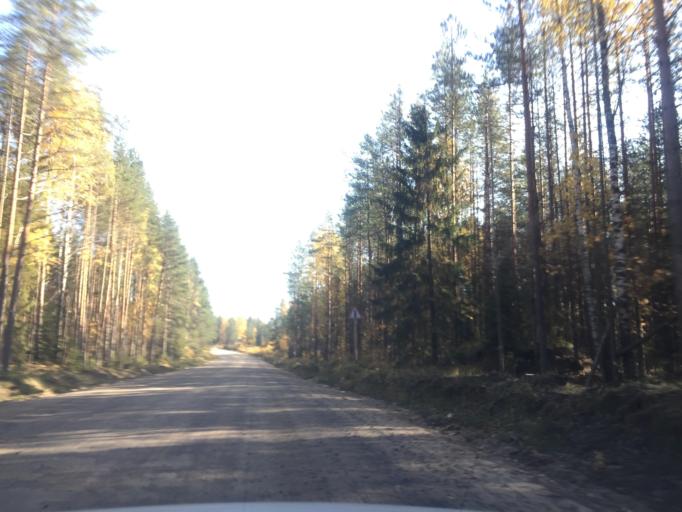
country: RU
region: Leningrad
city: Kuznechnoye
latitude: 61.3127
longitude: 30.0180
